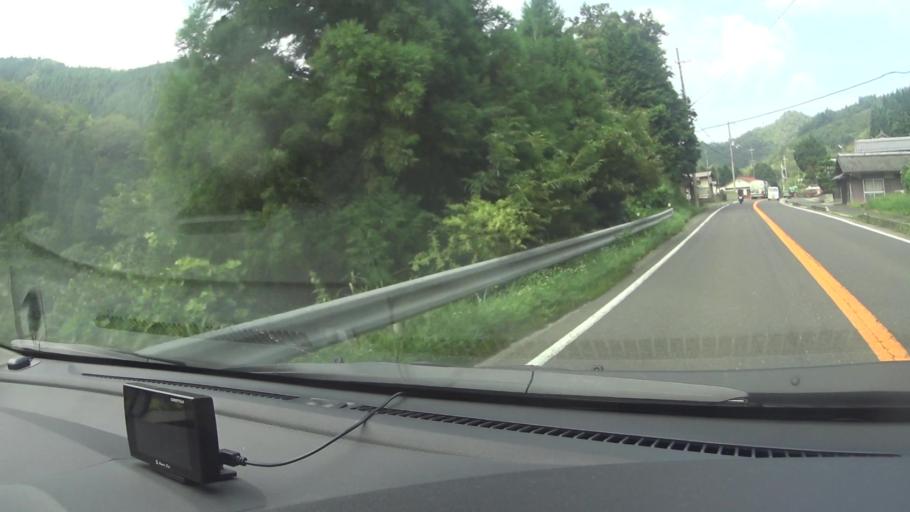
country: JP
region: Kyoto
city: Ayabe
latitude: 35.2475
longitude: 135.2815
